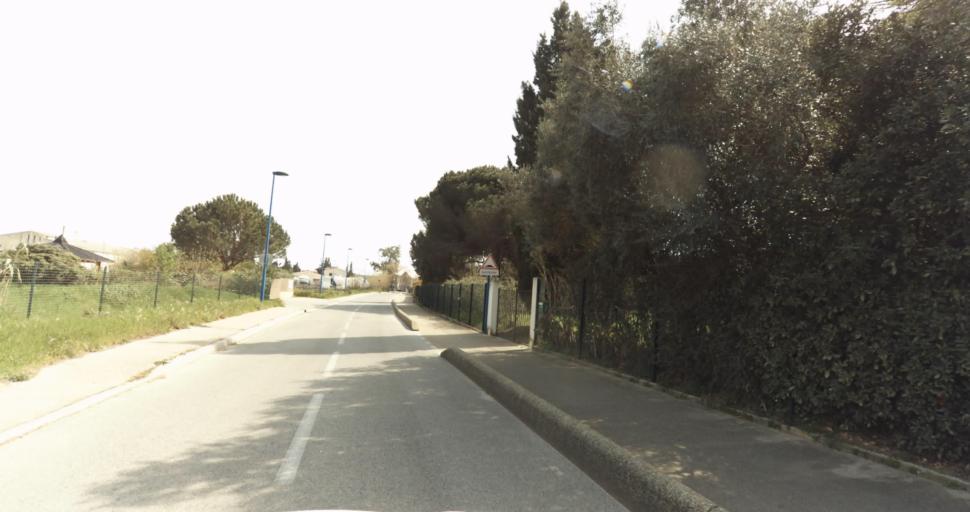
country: FR
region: Provence-Alpes-Cote d'Azur
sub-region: Departement du Var
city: Bormes-les-Mimosas
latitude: 43.1329
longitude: 6.3449
